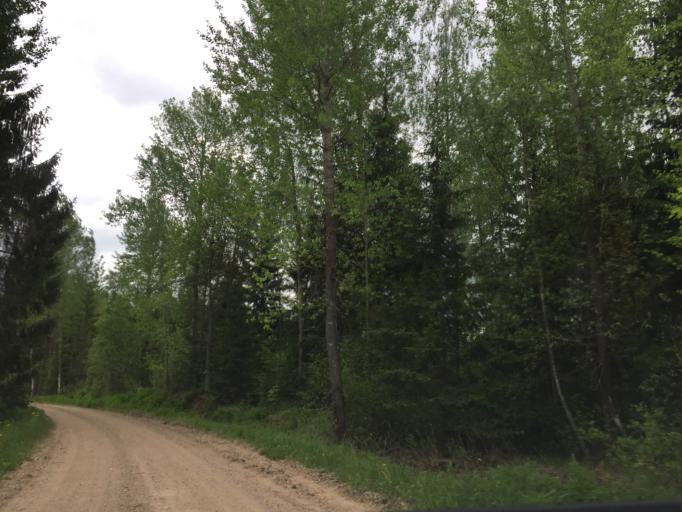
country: LV
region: Aglona
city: Aglona
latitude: 56.1771
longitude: 27.2507
